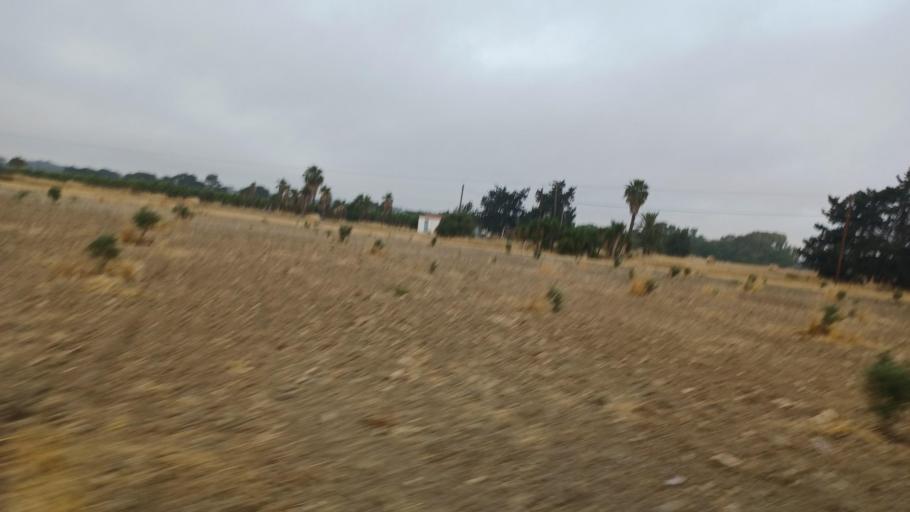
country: CY
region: Larnaka
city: Tersefanou
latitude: 34.8327
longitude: 33.5100
